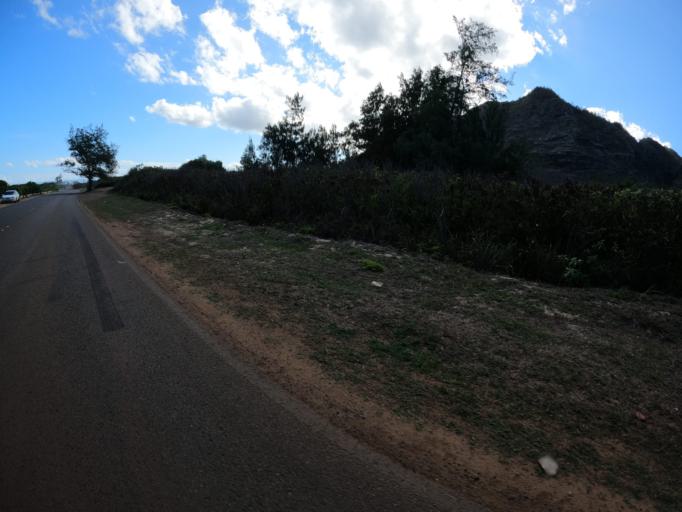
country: US
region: Hawaii
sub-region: Honolulu County
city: Mokuleia
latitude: 21.5788
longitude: -158.2167
